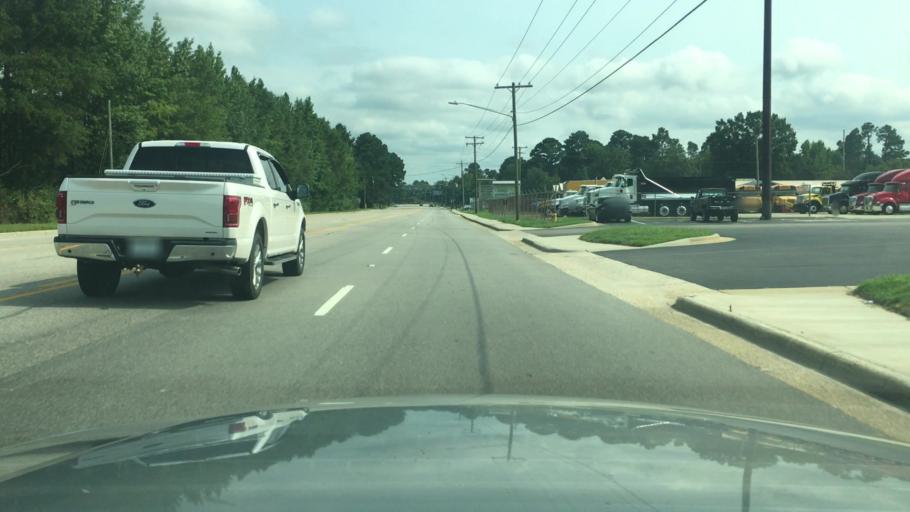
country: US
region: North Carolina
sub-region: Cumberland County
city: Fayetteville
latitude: 35.0293
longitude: -78.8439
